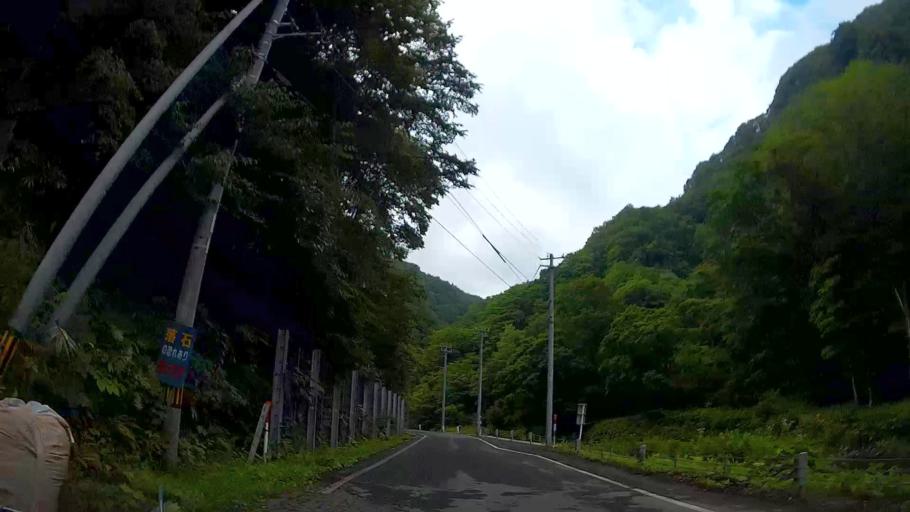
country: JP
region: Hokkaido
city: Nanae
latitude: 42.0762
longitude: 140.5273
